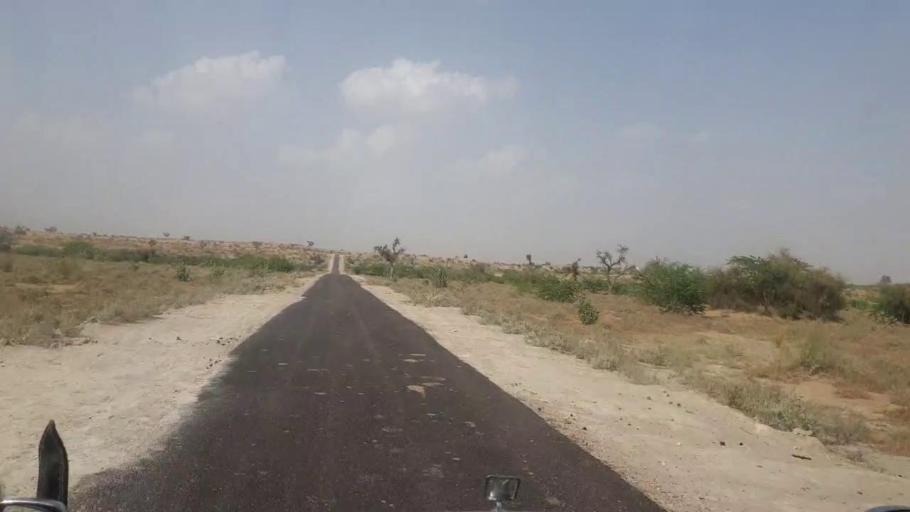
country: PK
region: Sindh
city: Islamkot
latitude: 25.2055
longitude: 70.2834
